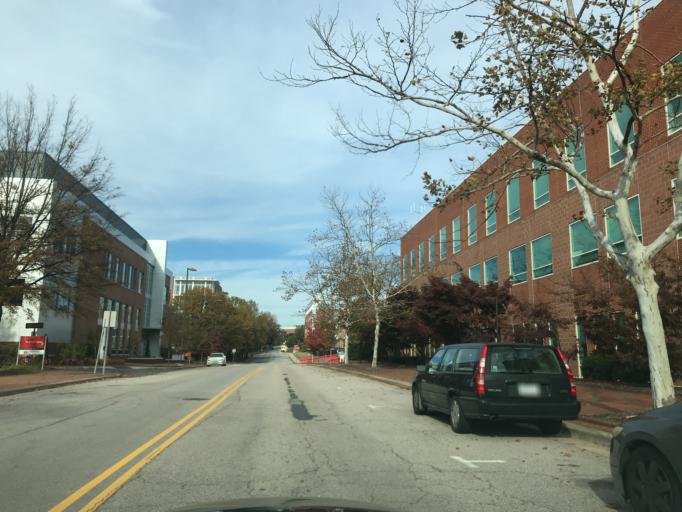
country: US
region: North Carolina
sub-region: Wake County
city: West Raleigh
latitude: 35.7703
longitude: -78.6778
